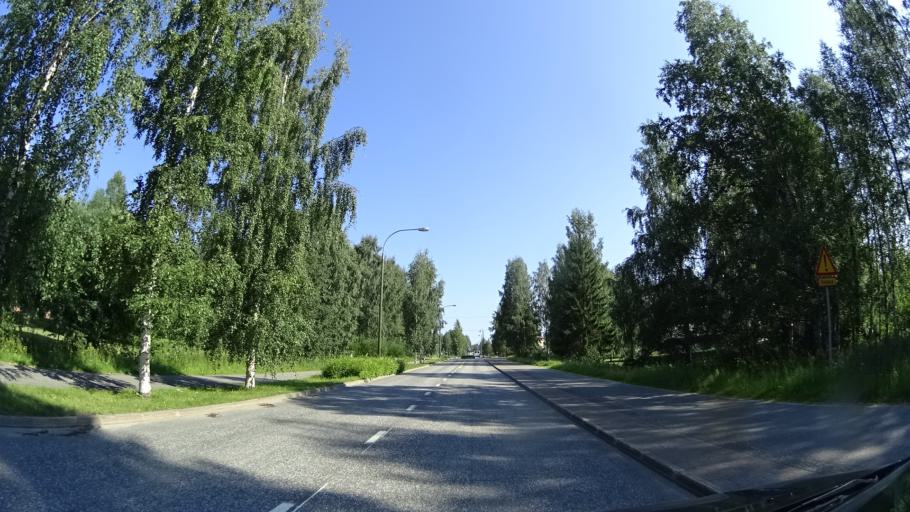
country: FI
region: North Karelia
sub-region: Joensuu
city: Juuka
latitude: 63.2362
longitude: 29.2472
